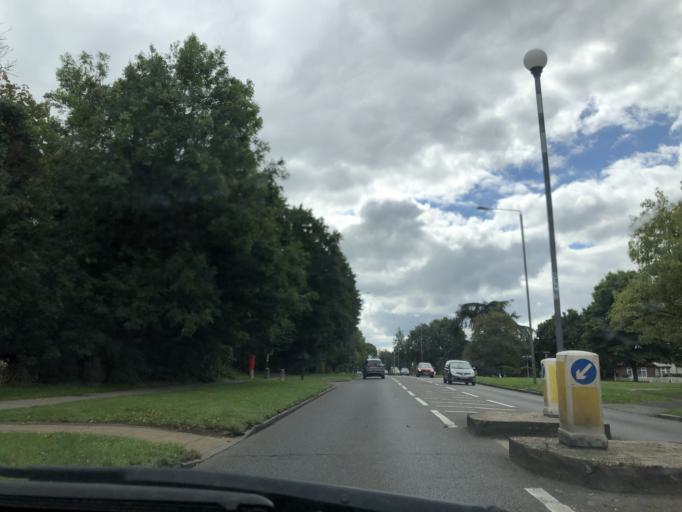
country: GB
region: England
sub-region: Greater London
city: Orpington
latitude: 51.3683
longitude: 0.1097
